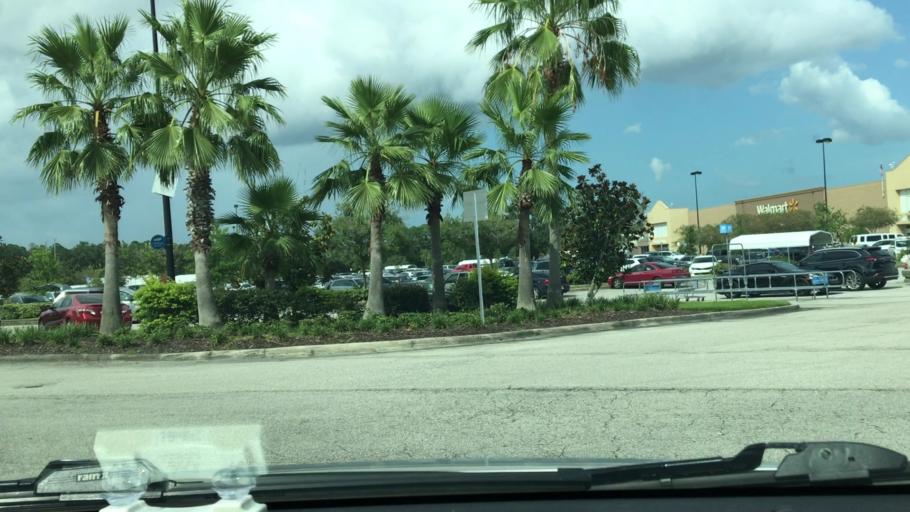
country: US
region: Florida
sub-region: Seminole County
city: Lake Mary
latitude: 28.8024
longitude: -81.3301
